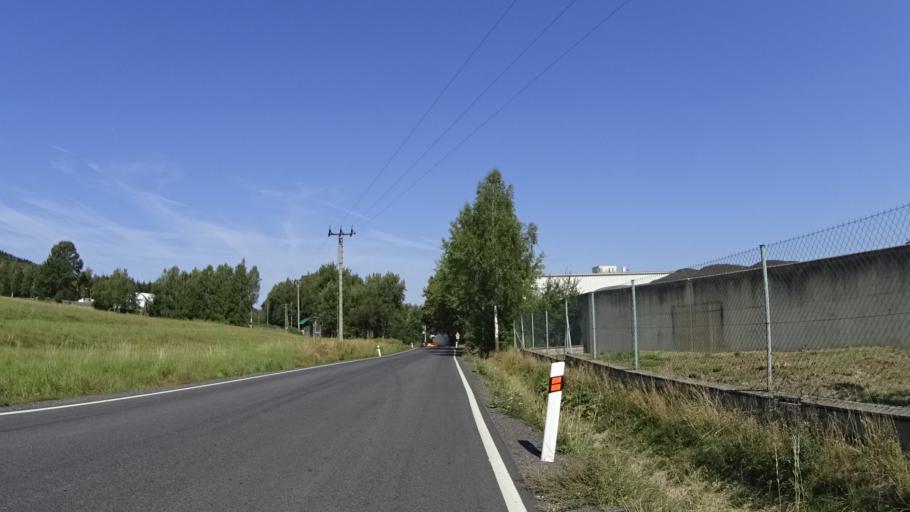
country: CZ
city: Chrastava
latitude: 50.8004
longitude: 14.9838
